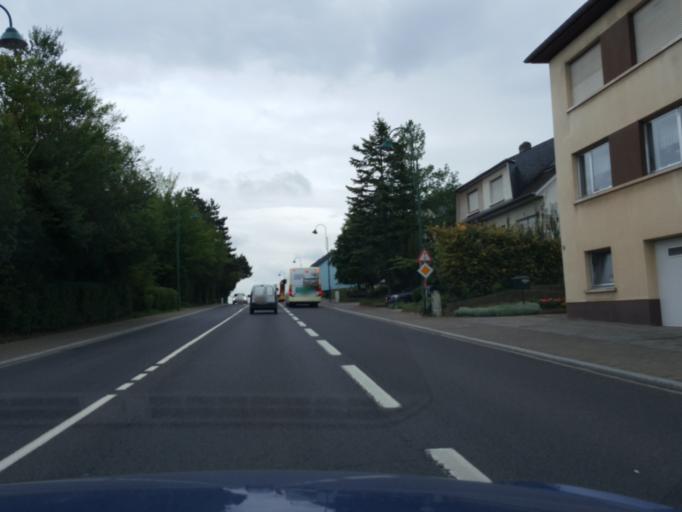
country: LU
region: Luxembourg
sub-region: Canton de Capellen
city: Mamer
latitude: 49.6335
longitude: 6.0179
